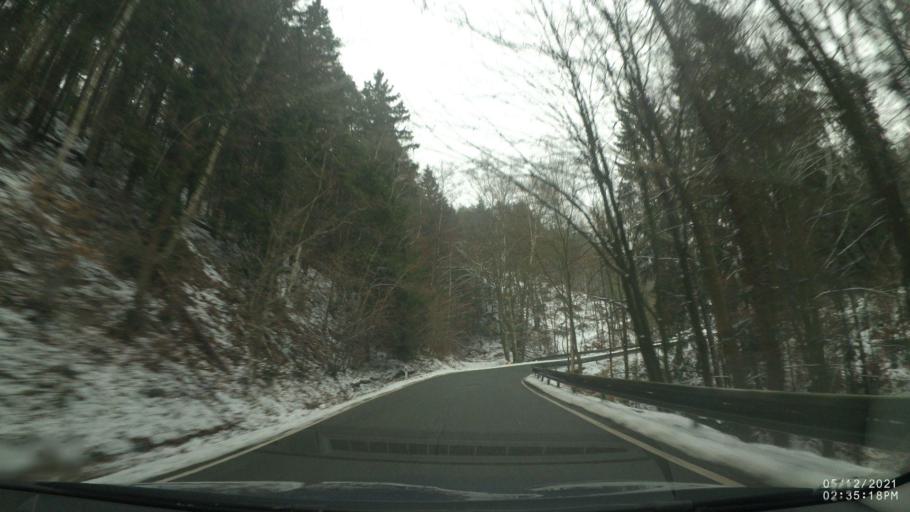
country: CZ
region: Kralovehradecky
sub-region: Okres Nachod
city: Nachod
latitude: 50.4005
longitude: 16.1726
